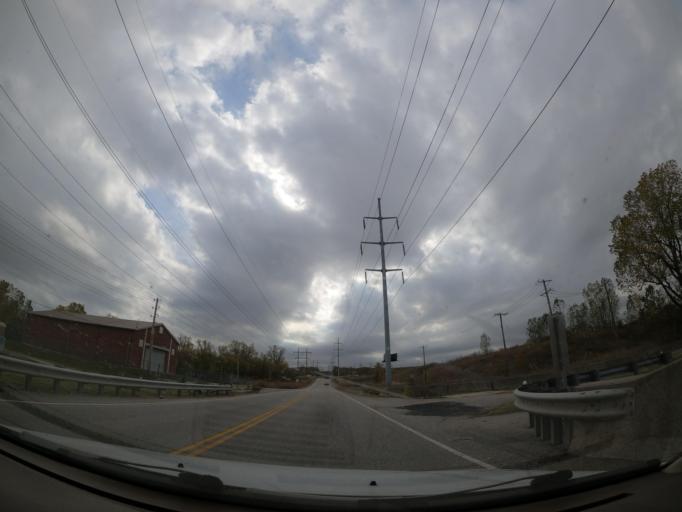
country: US
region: Oklahoma
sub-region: Tulsa County
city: Tulsa
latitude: 36.0930
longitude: -95.9937
